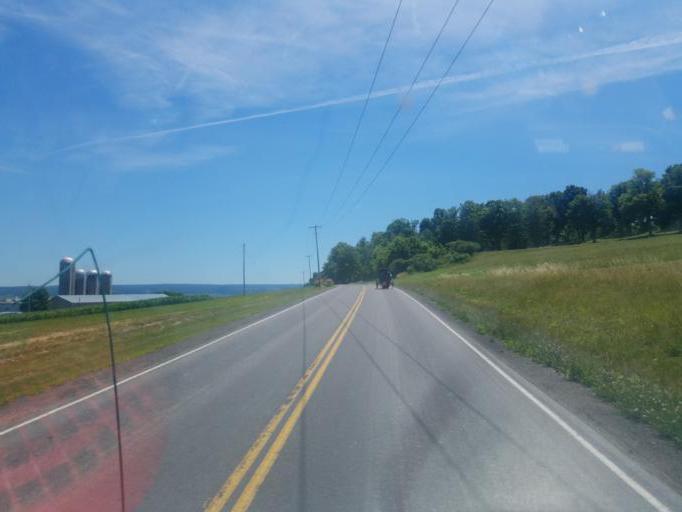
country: US
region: New York
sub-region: Yates County
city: Dundee
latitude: 42.5999
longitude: -76.9667
